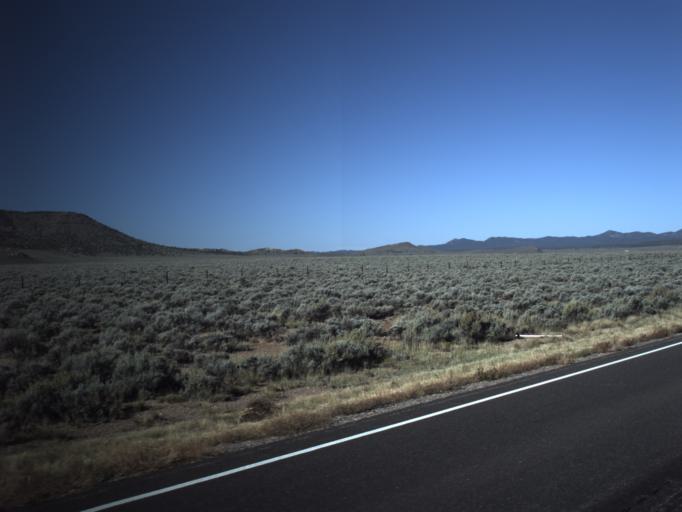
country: US
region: Utah
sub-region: Washington County
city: Enterprise
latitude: 37.7889
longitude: -113.8829
